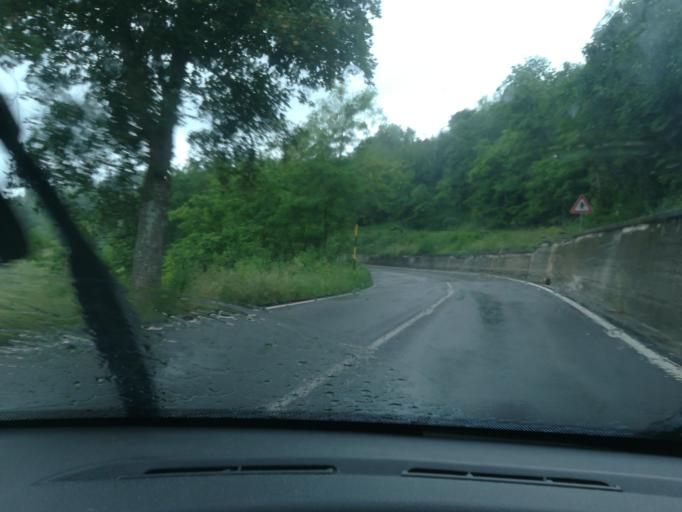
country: IT
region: The Marches
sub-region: Province of Fermo
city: Amandola
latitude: 43.0071
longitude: 13.3276
